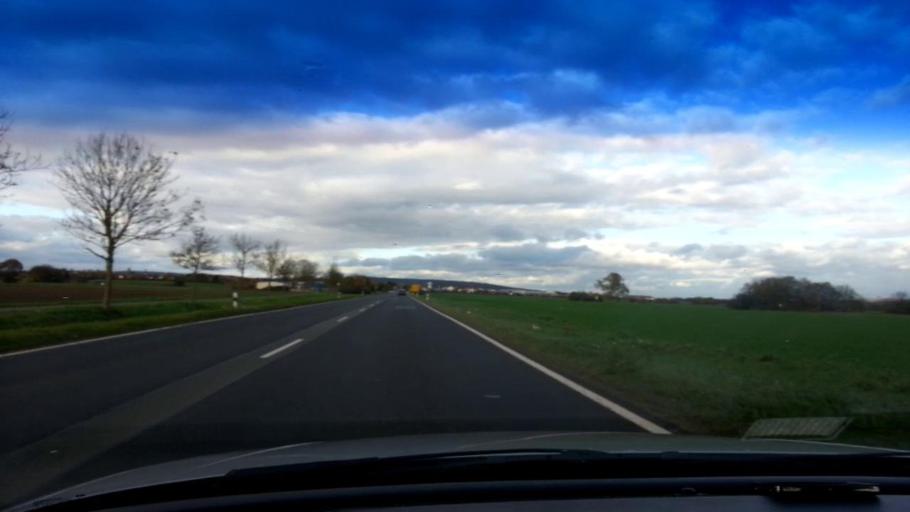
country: DE
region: Bavaria
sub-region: Upper Franconia
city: Rattelsdorf
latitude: 50.0004
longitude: 10.8864
